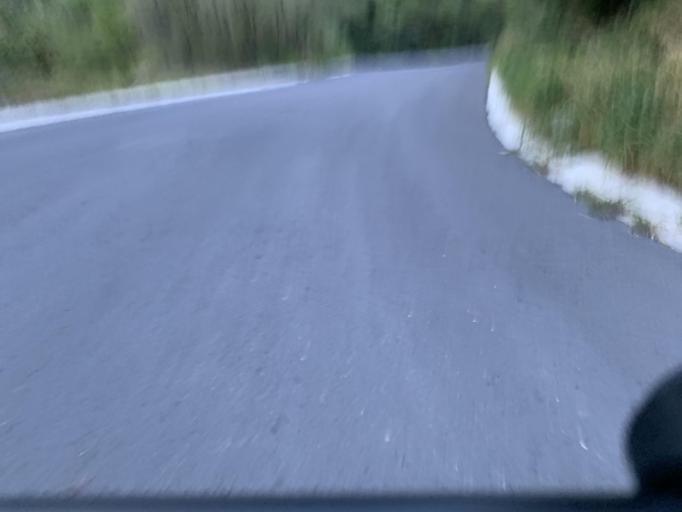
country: MX
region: Nuevo Leon
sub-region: Juarez
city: Bosques de San Pedro
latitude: 25.5206
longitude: -100.1873
